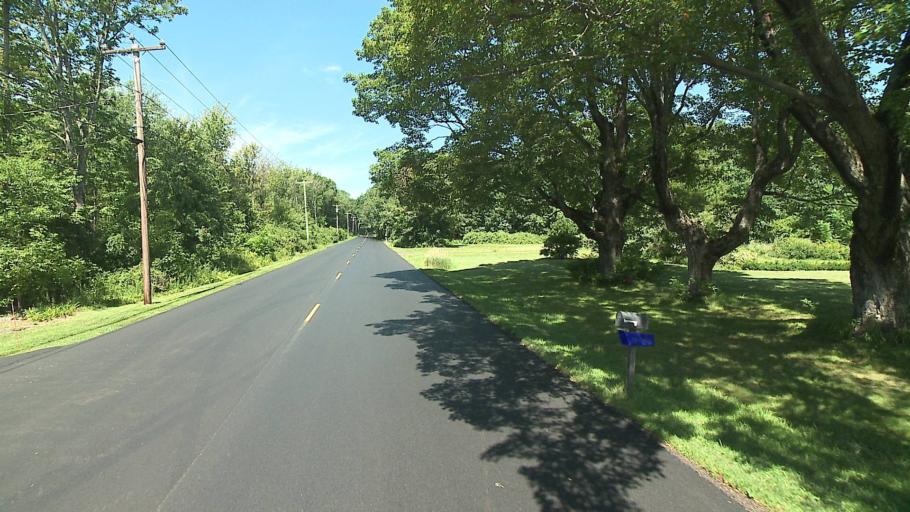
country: US
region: Connecticut
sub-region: Hartford County
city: West Simsbury
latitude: 41.9280
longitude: -72.9130
